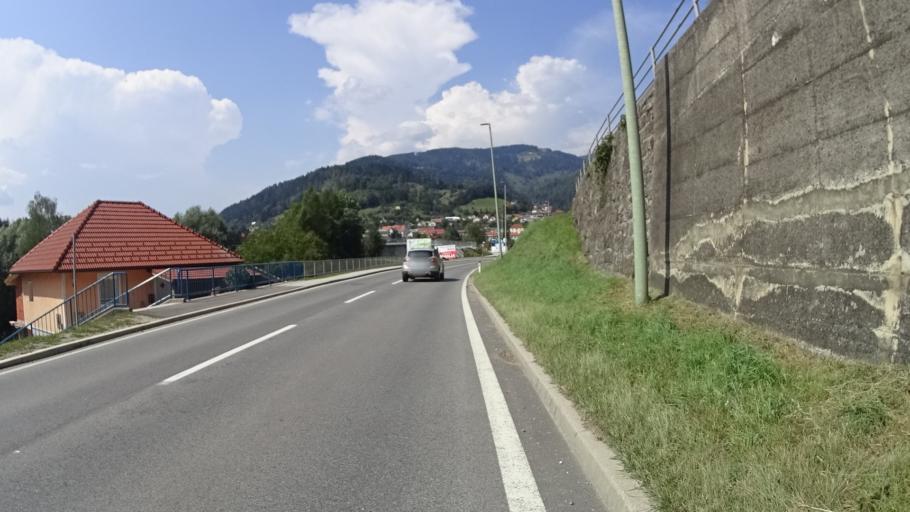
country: SI
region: Dravograd
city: Dravograd
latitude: 46.5838
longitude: 15.0231
